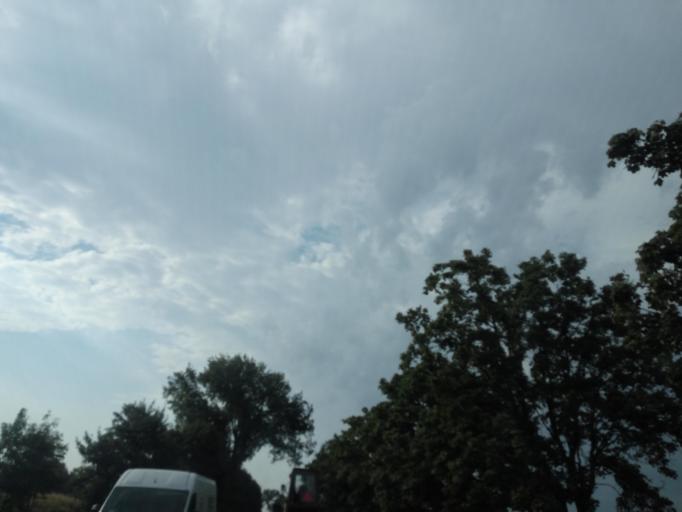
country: PL
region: Lower Silesian Voivodeship
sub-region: Powiat wroclawski
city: Zerniki Wroclawskie
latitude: 51.0041
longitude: 17.0649
